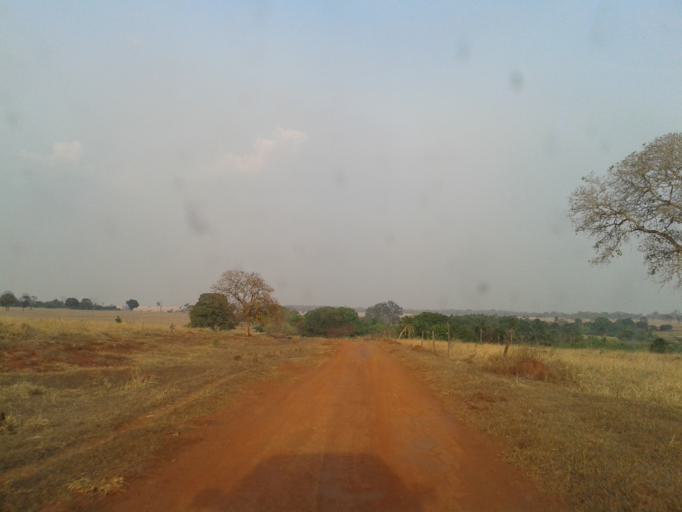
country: BR
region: Minas Gerais
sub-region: Capinopolis
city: Capinopolis
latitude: -18.8081
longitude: -49.7352
